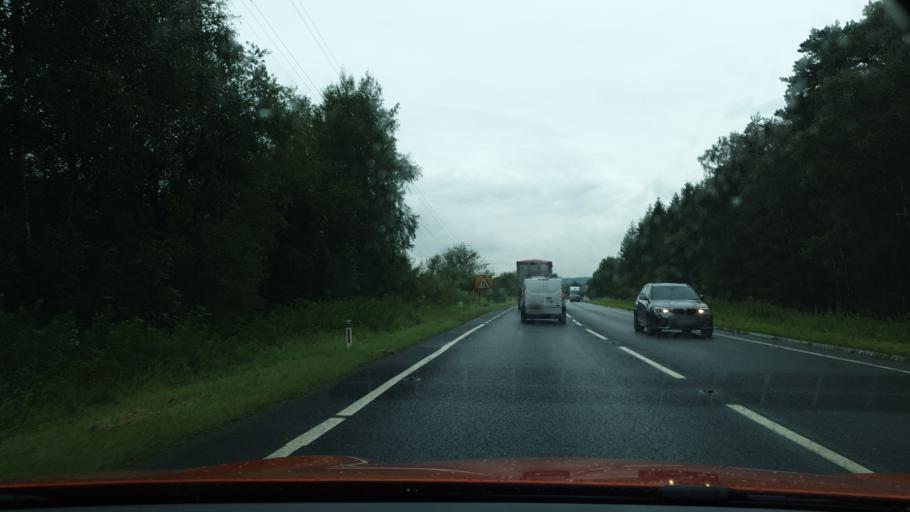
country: GB
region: England
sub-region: Cumbria
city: Arnside
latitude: 54.2538
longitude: -2.8287
